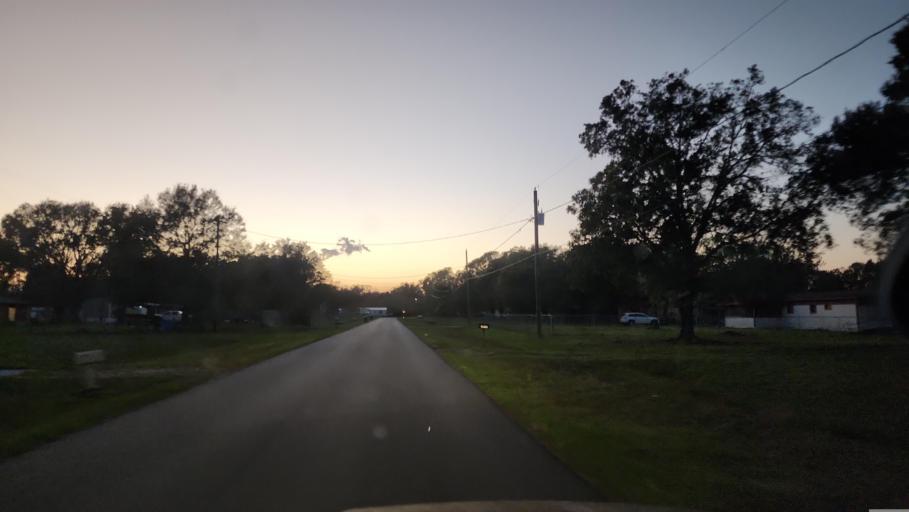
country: US
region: Florida
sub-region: Hillsborough County
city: Boyette
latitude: 27.8132
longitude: -82.2761
